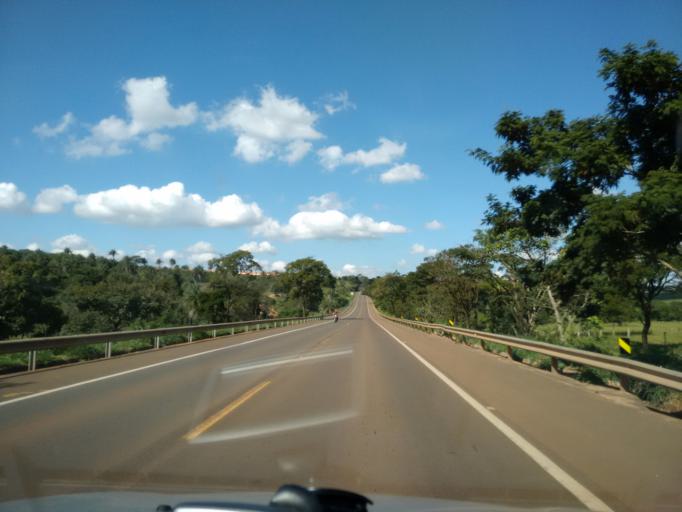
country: BR
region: Sao Paulo
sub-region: Sao Carlos
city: Sao Carlos
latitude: -22.0660
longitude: -47.9153
